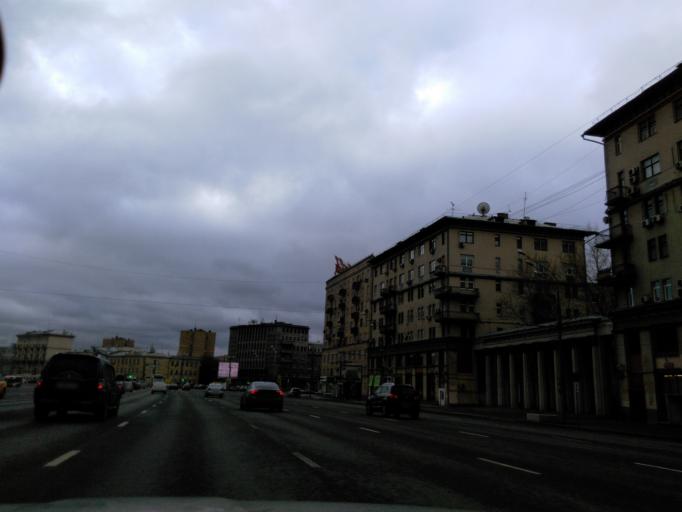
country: RU
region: Moskovskaya
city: Dorogomilovo
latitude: 55.7404
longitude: 37.5849
